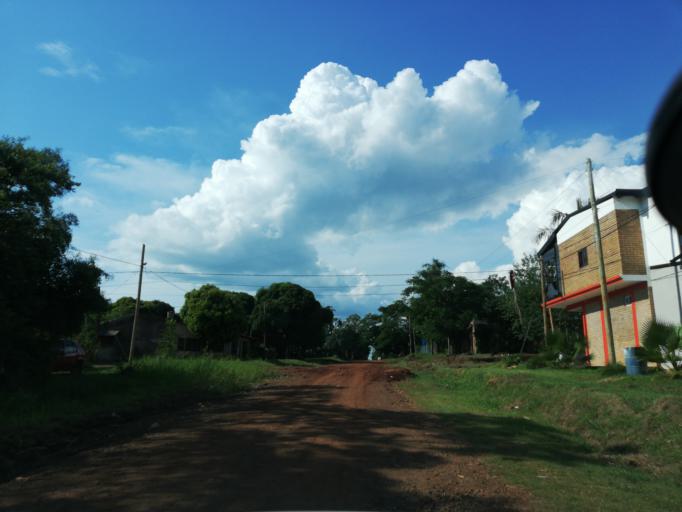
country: AR
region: Misiones
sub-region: Departamento de Capital
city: Posadas
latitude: -27.3897
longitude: -55.9235
